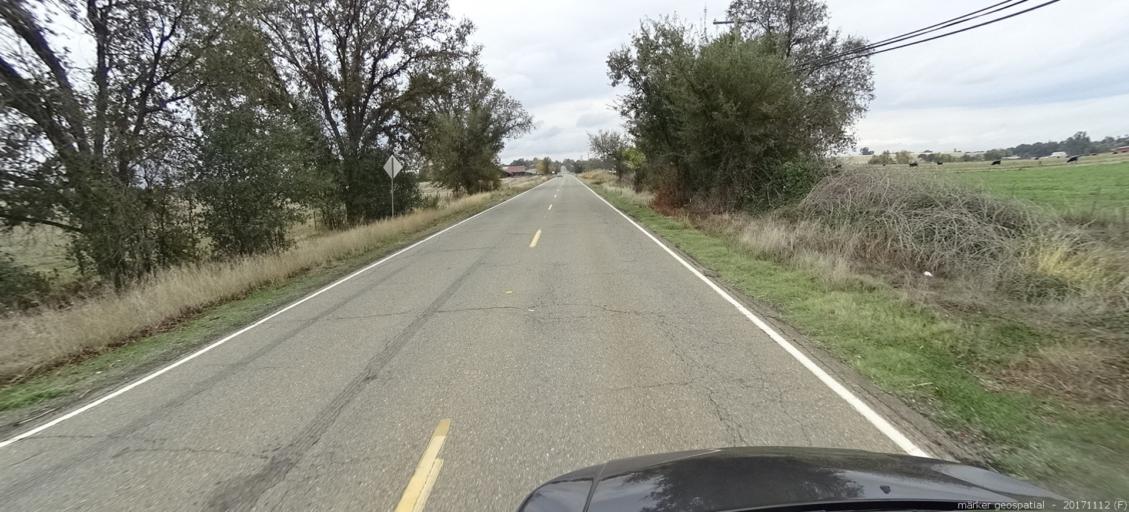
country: US
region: California
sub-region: Shasta County
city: Anderson
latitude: 40.4765
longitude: -122.2319
